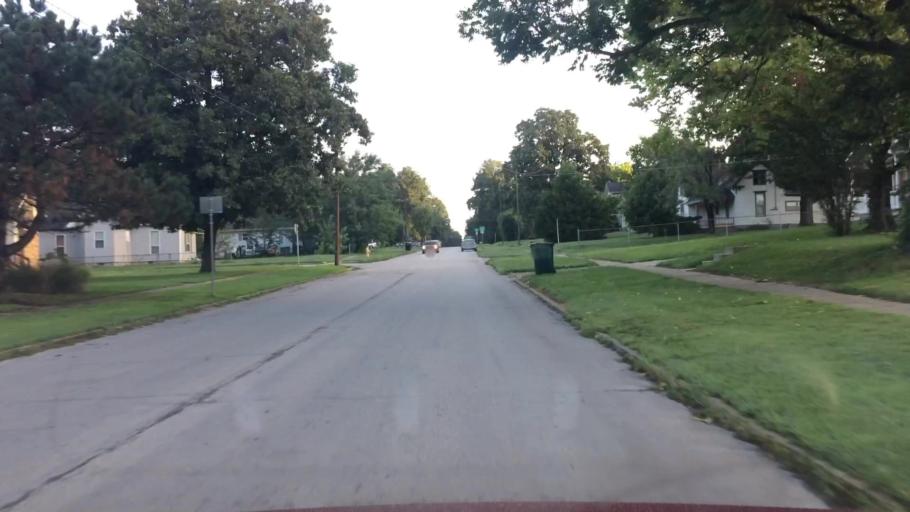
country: US
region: Missouri
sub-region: Greene County
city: Springfield
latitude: 37.2196
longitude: -93.2810
